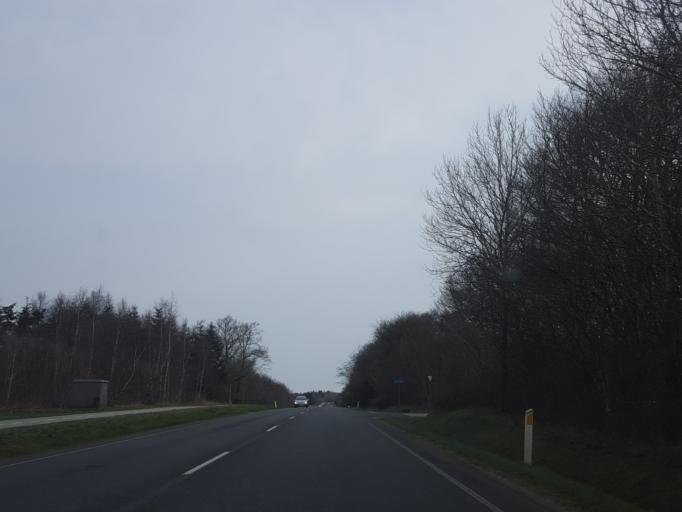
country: DK
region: South Denmark
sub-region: Varde Kommune
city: Varde
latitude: 55.5775
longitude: 8.4920
